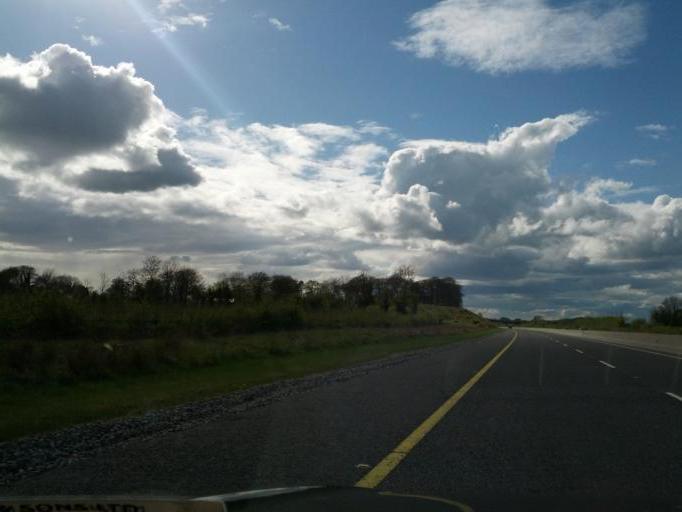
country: IE
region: Leinster
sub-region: Uibh Fhaili
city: Clara
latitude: 53.3818
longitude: -7.5726
